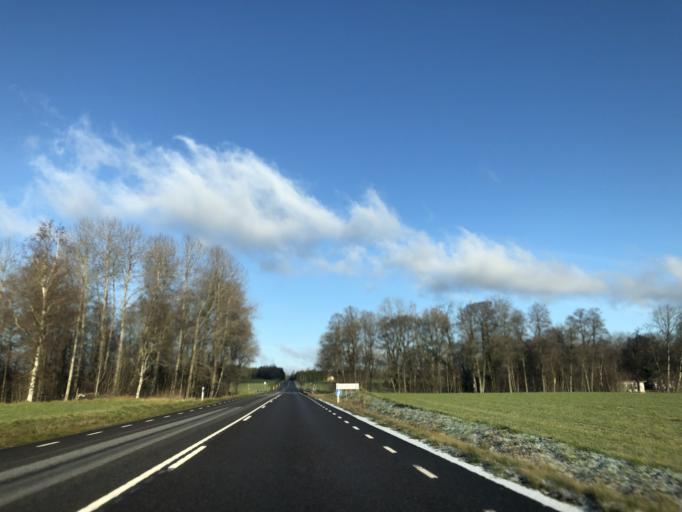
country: SE
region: Vaestra Goetaland
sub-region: Tranemo Kommun
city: Limmared
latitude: 57.6332
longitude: 13.4462
